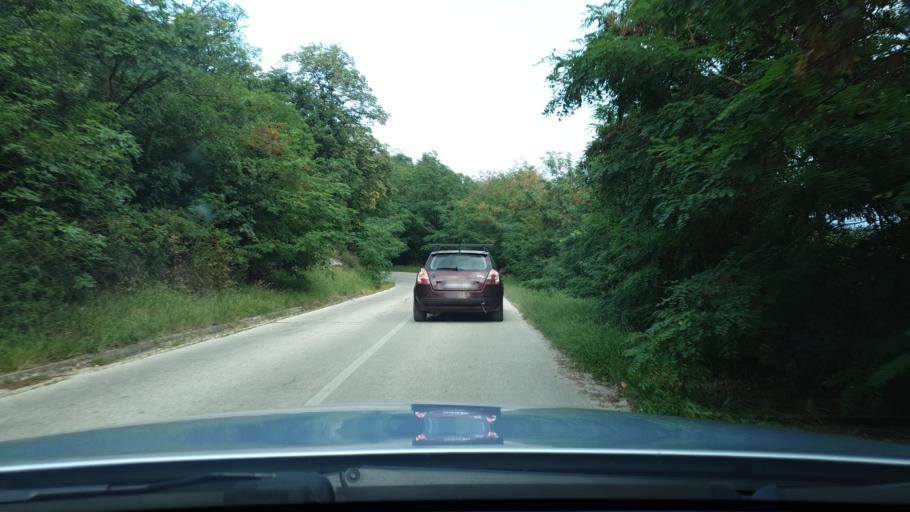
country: RS
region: Autonomna Pokrajina Vojvodina
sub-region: Juznobanatski Okrug
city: Vrsac
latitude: 45.1201
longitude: 21.3251
